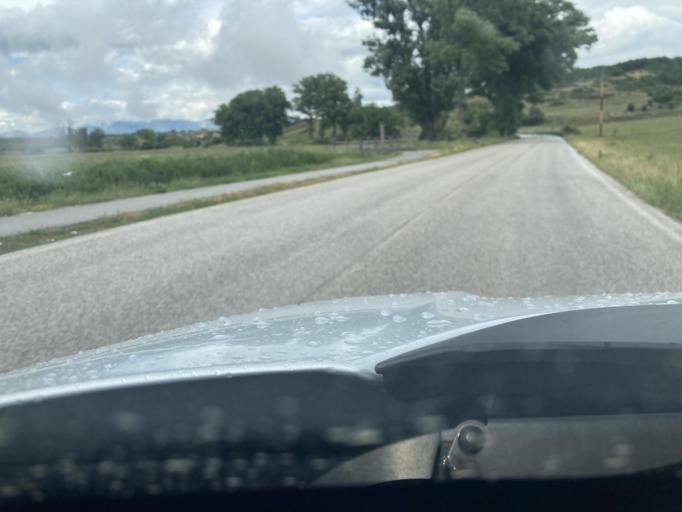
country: IT
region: Abruzzo
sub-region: Provincia dell' Aquila
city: Rocca di Mezzo
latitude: 42.2209
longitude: 13.5325
